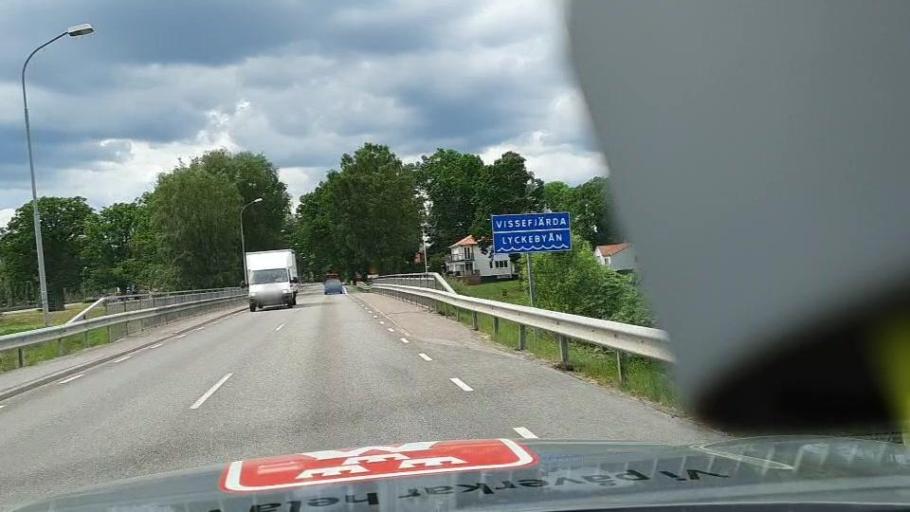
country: SE
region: Kalmar
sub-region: Emmaboda Kommun
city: Emmaboda
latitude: 56.5348
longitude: 15.6021
